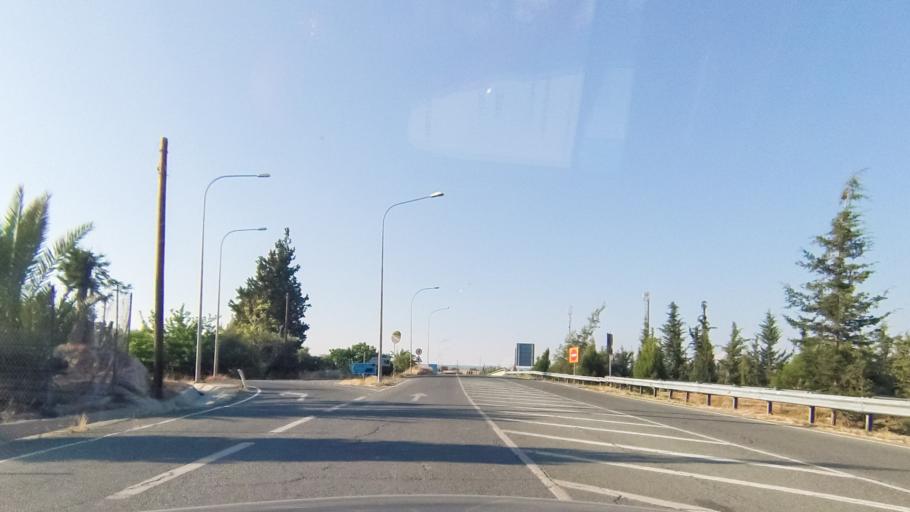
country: CY
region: Limassol
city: Pissouri
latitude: 34.6814
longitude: 32.7603
